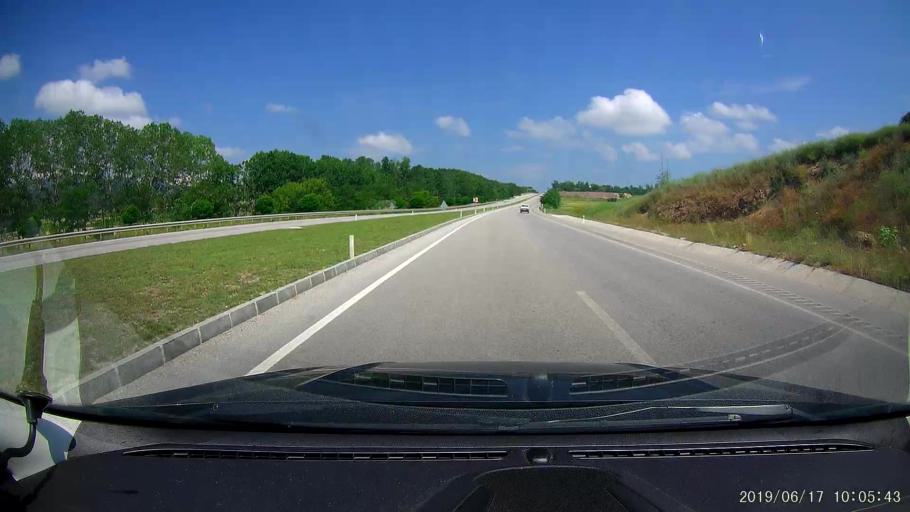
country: TR
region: Amasya
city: Gumushacikoy
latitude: 40.8978
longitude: 35.1862
